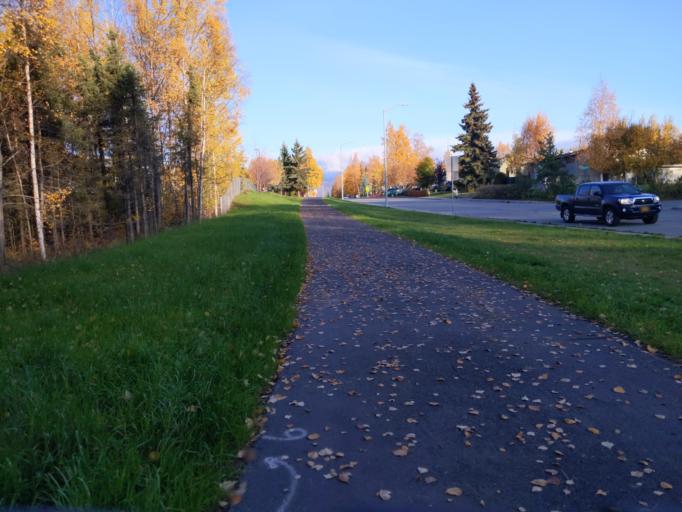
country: US
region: Alaska
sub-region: Anchorage Municipality
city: Anchorage
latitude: 61.1557
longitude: -149.8723
